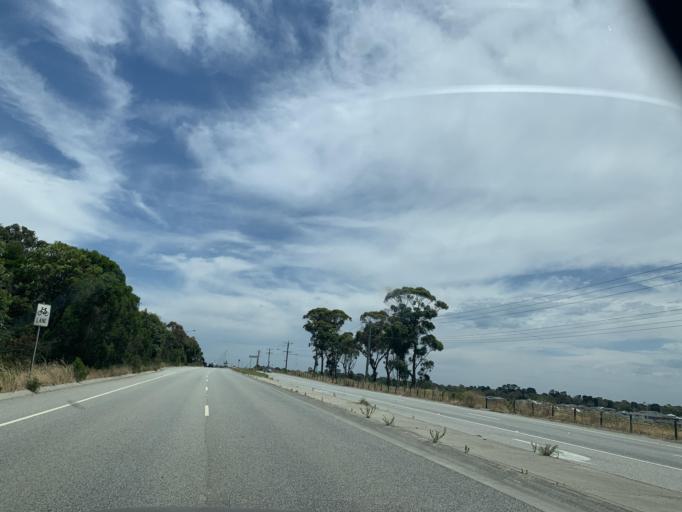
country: AU
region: Victoria
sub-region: Casey
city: Cranbourne South
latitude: -38.1291
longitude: 145.2390
